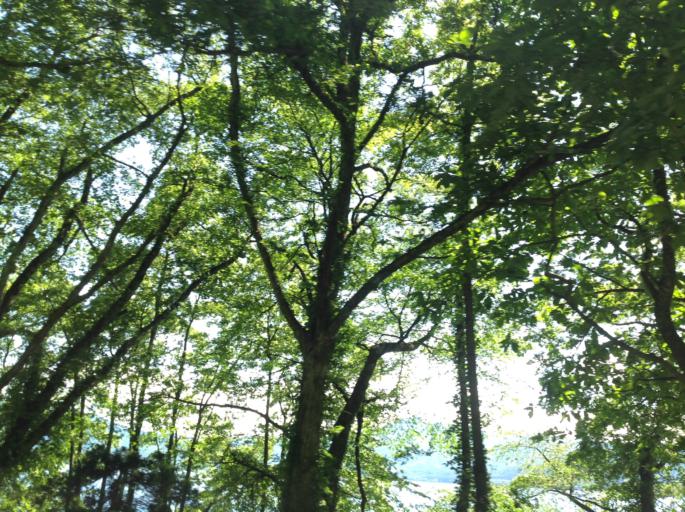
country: JP
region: Akita
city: Kakunodatemachi
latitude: 39.7059
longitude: 140.6405
